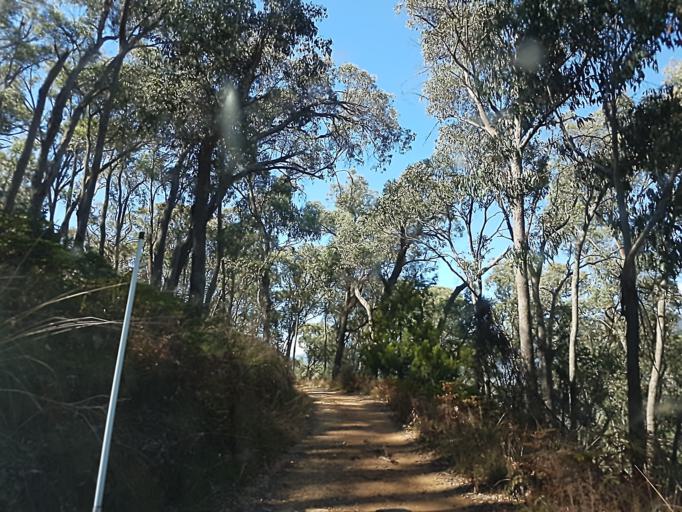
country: AU
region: Victoria
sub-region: Alpine
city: Mount Beauty
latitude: -36.8814
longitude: 147.0385
